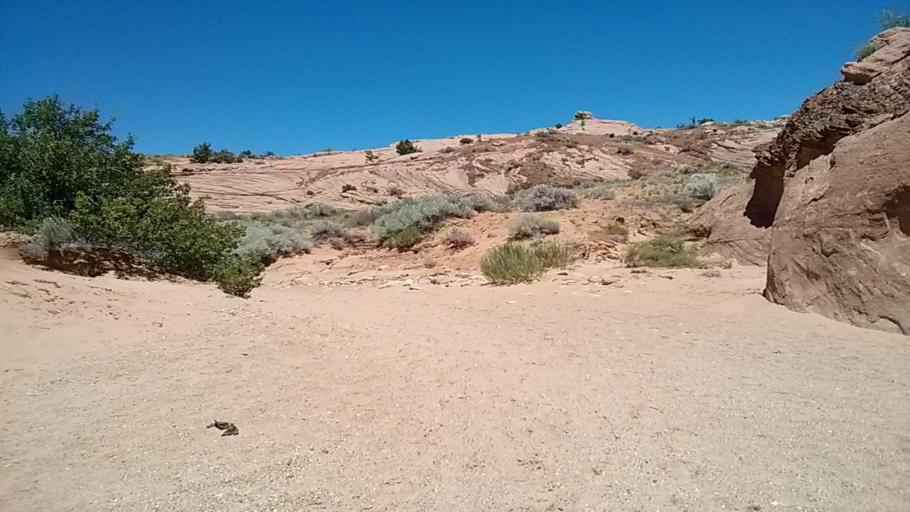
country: US
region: Arizona
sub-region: Coconino County
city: Page
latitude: 37.4798
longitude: -111.2119
